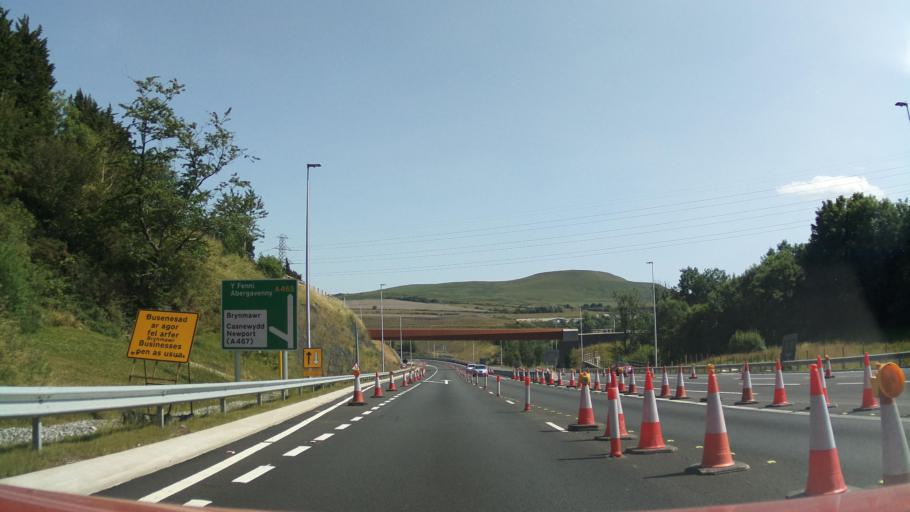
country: GB
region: Wales
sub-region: Blaenau Gwent
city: Brynmawr
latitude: 51.8059
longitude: -3.1693
